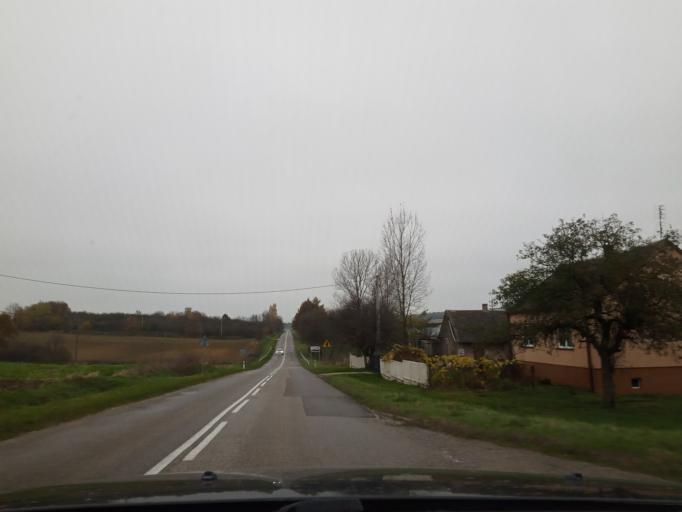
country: PL
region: Swietokrzyskie
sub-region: Powiat pinczowski
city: Dzialoszyce
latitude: 50.4367
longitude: 20.3492
